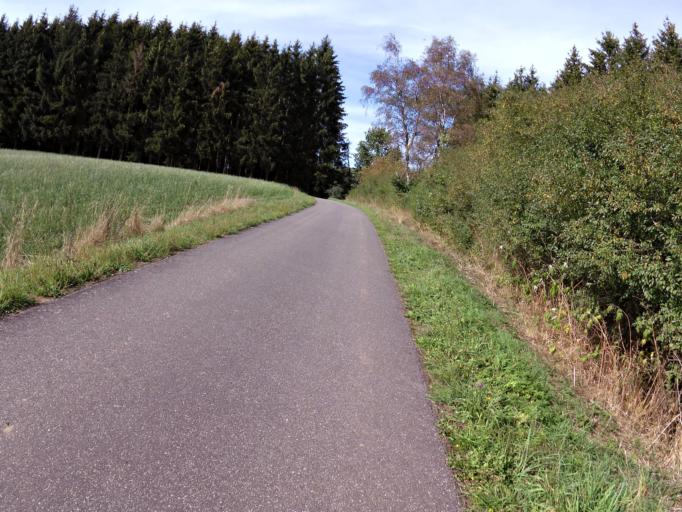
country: DE
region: Rheinland-Pfalz
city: Bleialf
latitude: 50.2099
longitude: 6.2829
